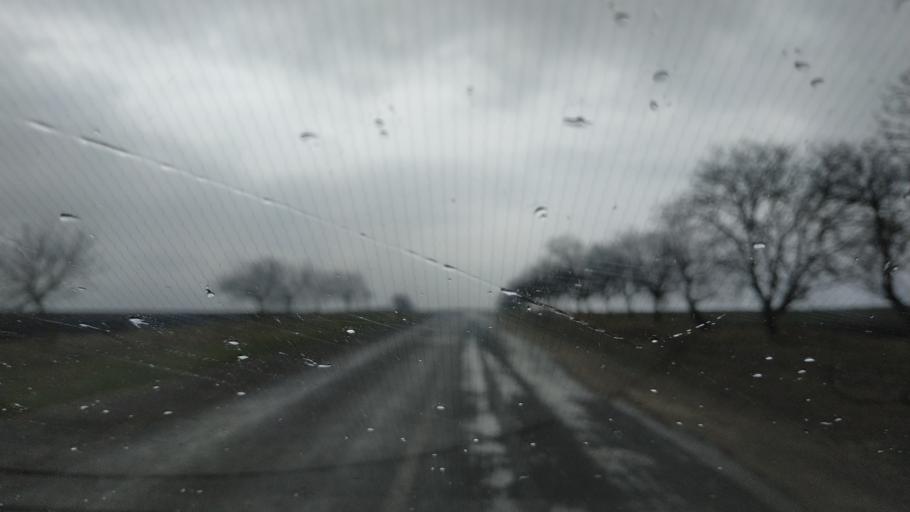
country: MD
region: Gagauzia
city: Comrat
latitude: 46.3080
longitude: 28.6095
